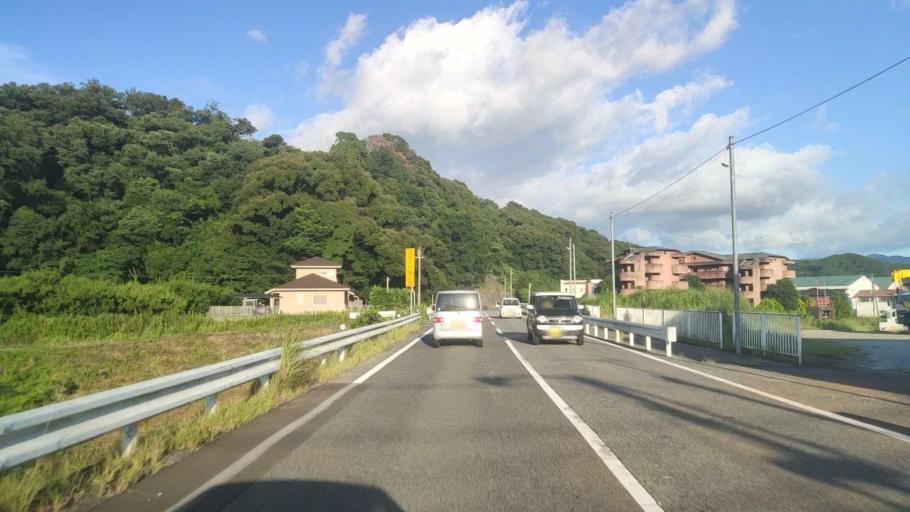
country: JP
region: Wakayama
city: Tanabe
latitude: 33.7263
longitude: 135.4425
